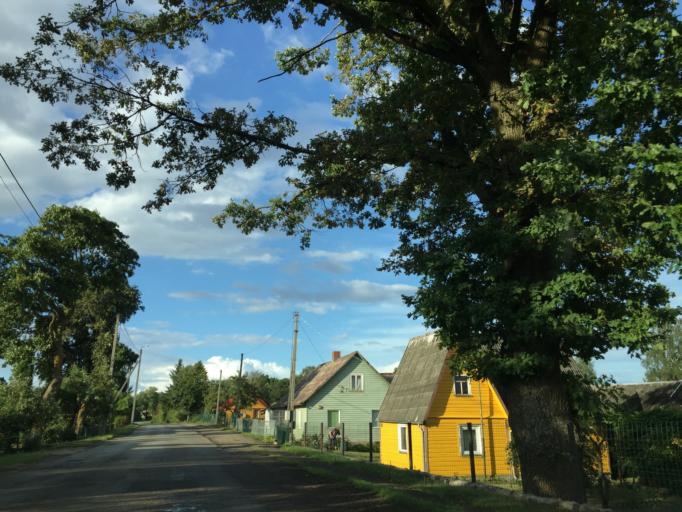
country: LT
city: Zagare
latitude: 56.3670
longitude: 23.2647
